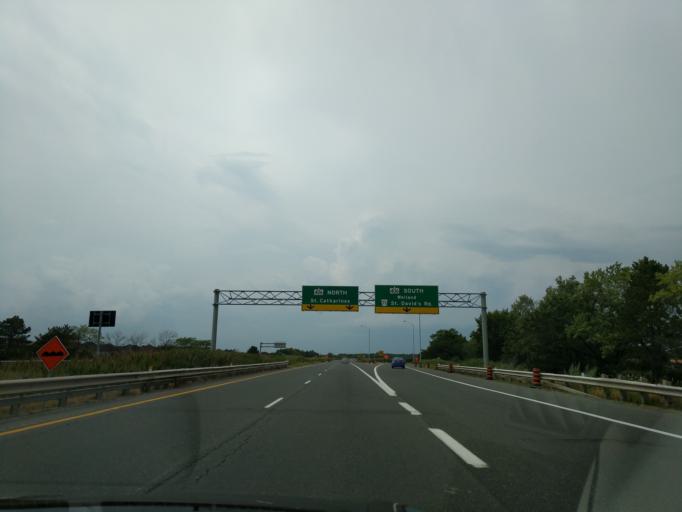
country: CA
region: Ontario
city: Thorold
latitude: 43.1171
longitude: -79.2225
